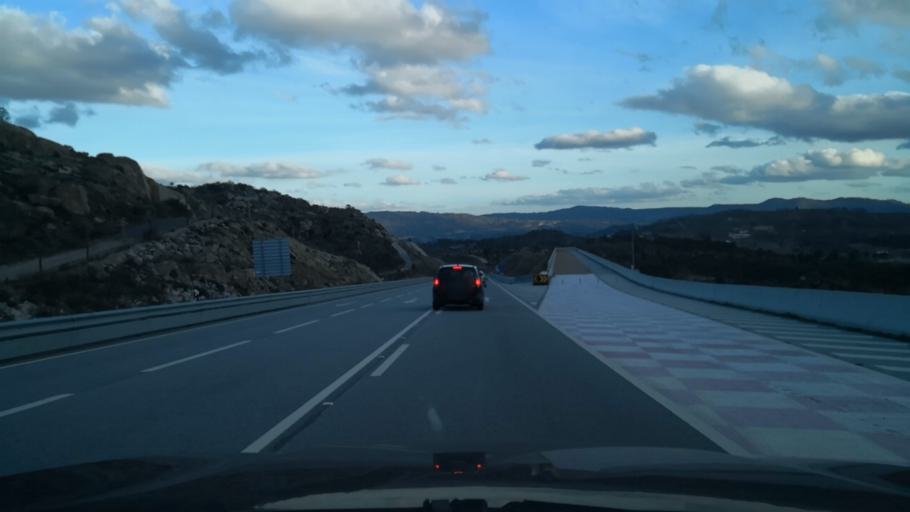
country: PT
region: Vila Real
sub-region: Murca
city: Murca
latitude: 41.3271
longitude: -7.4199
